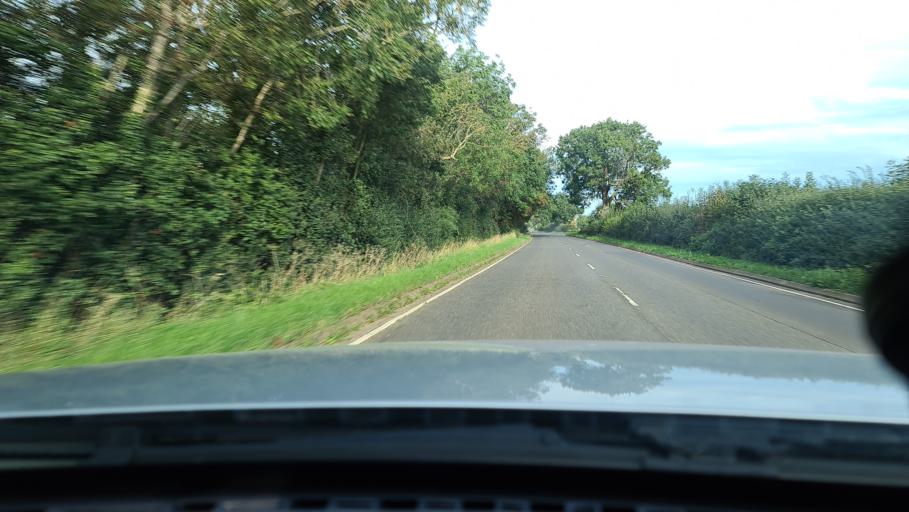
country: GB
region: England
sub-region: Warwickshire
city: Wellesbourne Mountford
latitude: 52.1144
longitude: -1.4869
